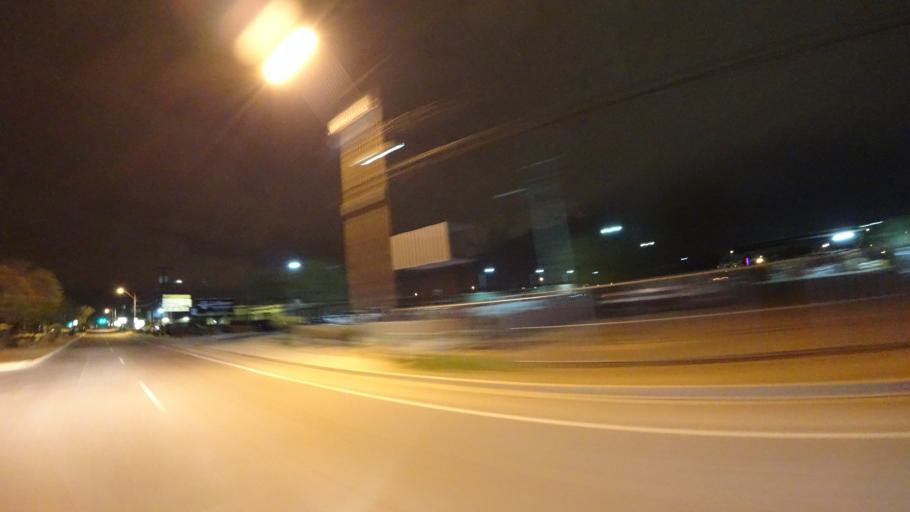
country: US
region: Arizona
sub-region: Maricopa County
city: Tempe
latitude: 33.4403
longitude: -111.9224
